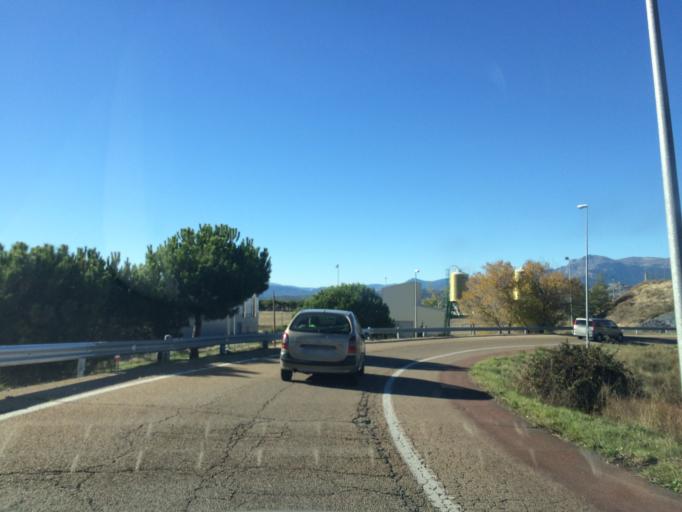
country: ES
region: Madrid
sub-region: Provincia de Madrid
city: Colmenar Viejo
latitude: 40.6837
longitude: -3.7856
